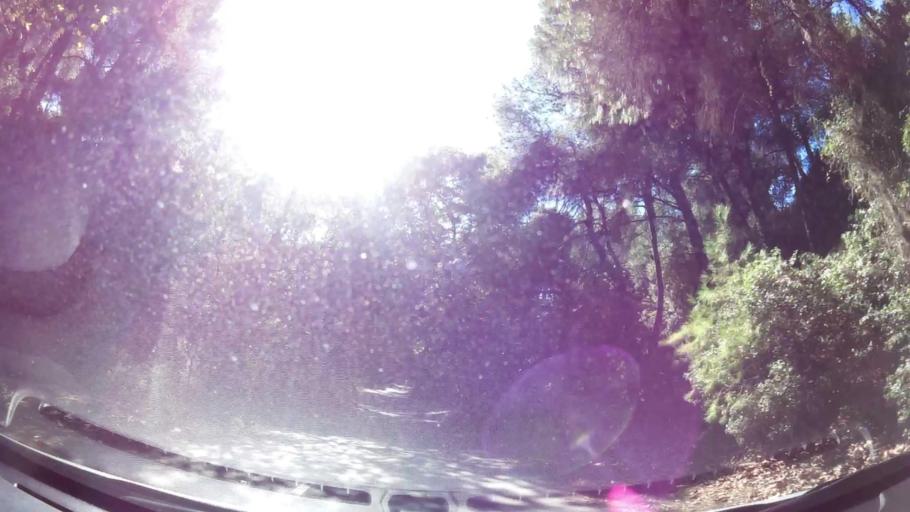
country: GR
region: Attica
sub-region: Nomarchia Anatolikis Attikis
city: Varybobi
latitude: 38.1310
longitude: 23.7870
